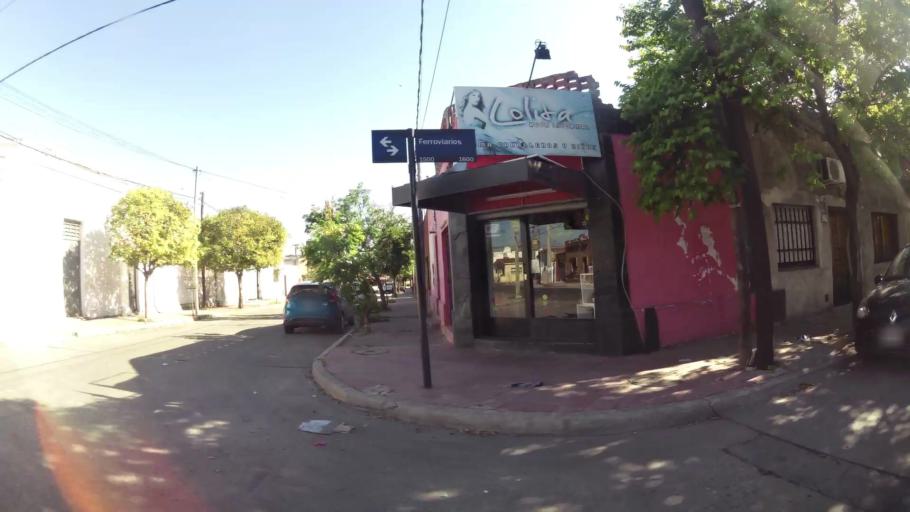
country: AR
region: Cordoba
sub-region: Departamento de Capital
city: Cordoba
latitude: -31.4290
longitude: -64.1650
